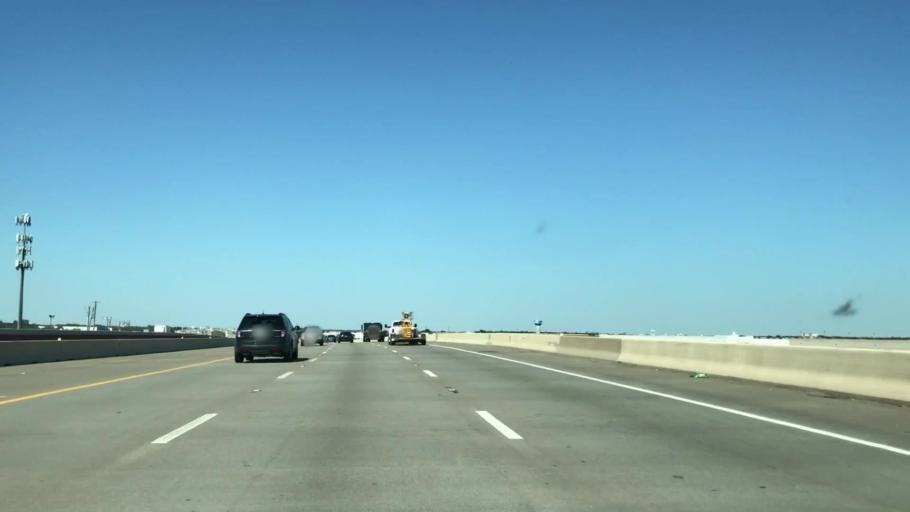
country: US
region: Texas
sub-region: Dallas County
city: Farmers Branch
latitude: 32.9253
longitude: -96.9312
